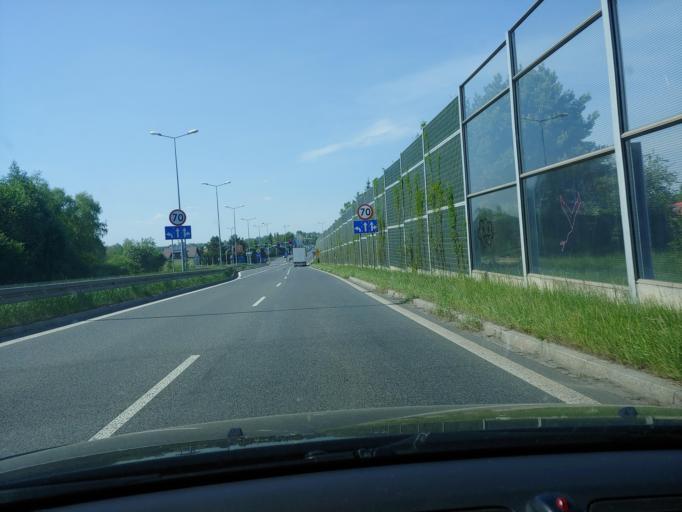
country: PL
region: Silesian Voivodeship
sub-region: Jaworzno
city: Jaworzno
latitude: 50.1787
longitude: 19.2924
